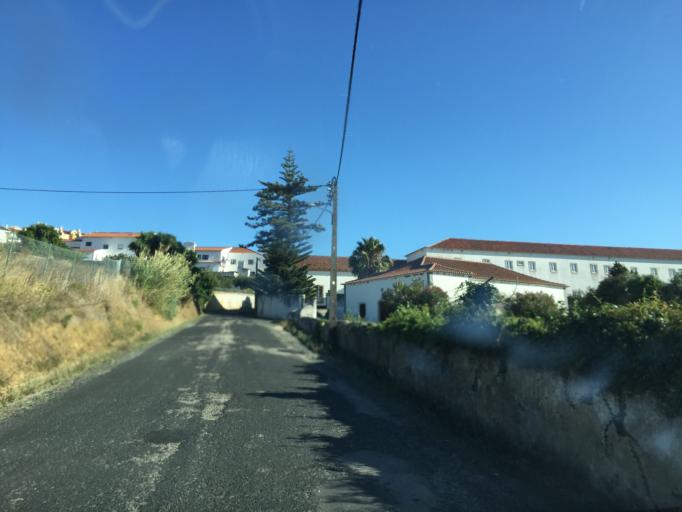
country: PT
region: Lisbon
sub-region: Torres Vedras
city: Torres Vedras
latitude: 39.0918
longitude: -9.2795
